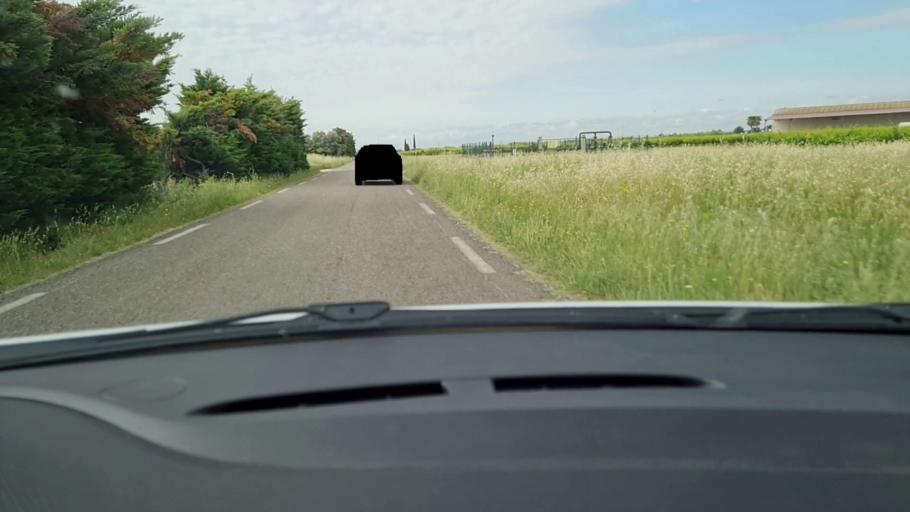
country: FR
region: Languedoc-Roussillon
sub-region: Departement du Gard
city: Bellegarde
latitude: 43.7713
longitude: 4.5175
